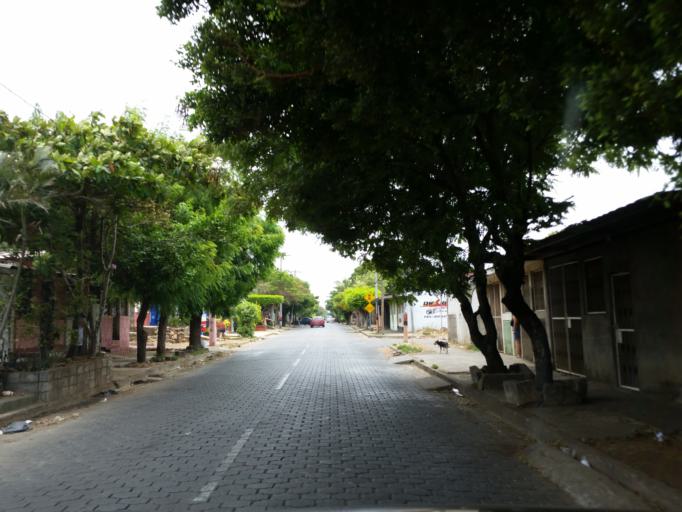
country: NI
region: Managua
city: Managua
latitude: 12.1282
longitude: -86.2491
